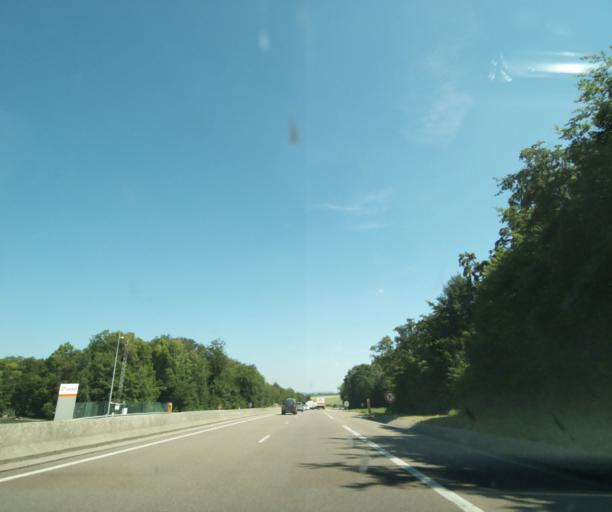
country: FR
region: Lorraine
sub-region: Departement de Meurthe-et-Moselle
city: Colombey-les-Belles
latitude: 48.4255
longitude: 5.8602
